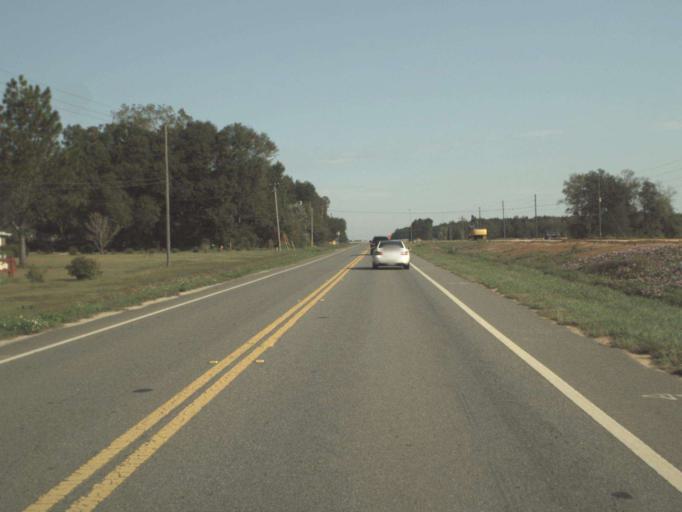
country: US
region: Florida
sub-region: Holmes County
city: Bonifay
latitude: 30.7532
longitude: -85.6849
